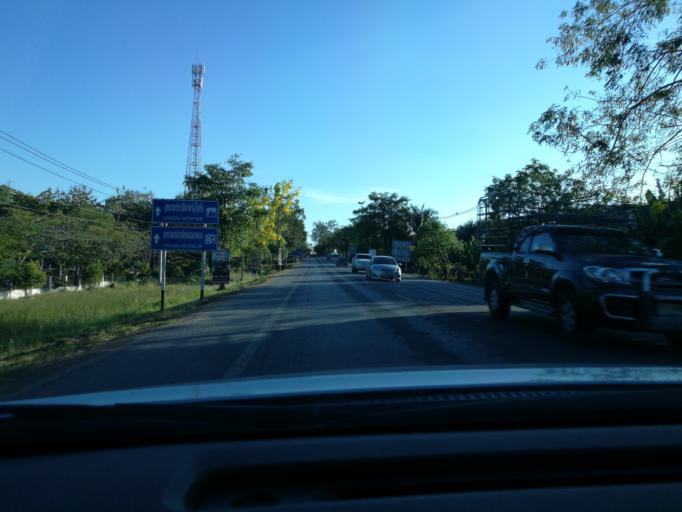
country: TH
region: Phitsanulok
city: Nakhon Thai
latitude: 17.0602
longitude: 100.8098
